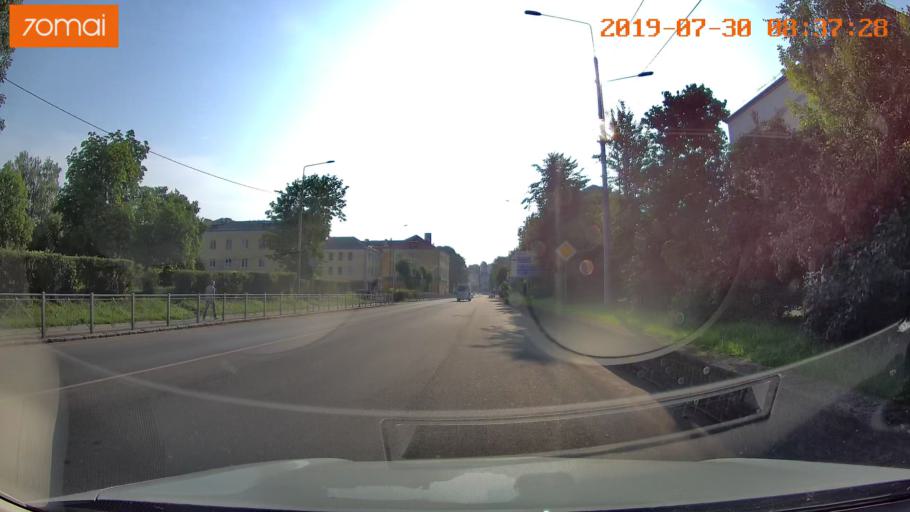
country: RU
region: Kaliningrad
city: Chernyakhovsk
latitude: 54.6358
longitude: 21.8006
